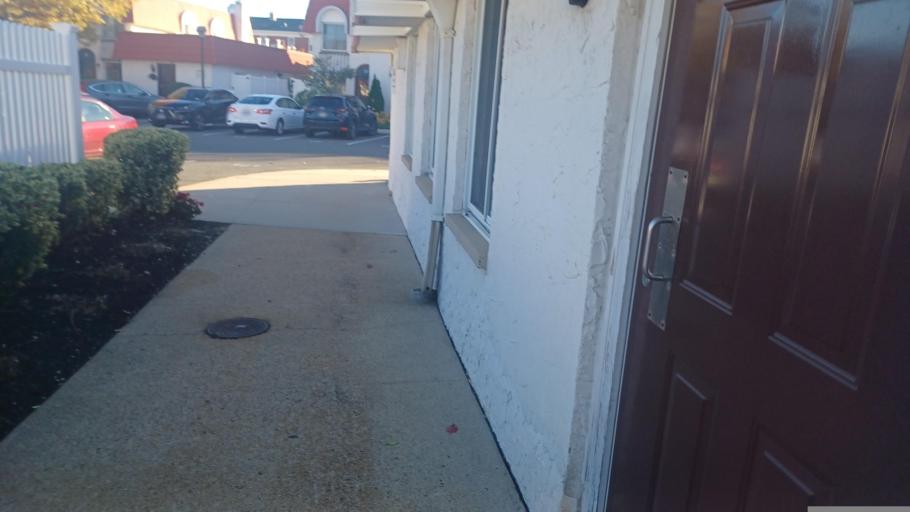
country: US
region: New York
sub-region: Nassau County
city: Oceanside
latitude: 40.6257
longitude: -73.6409
